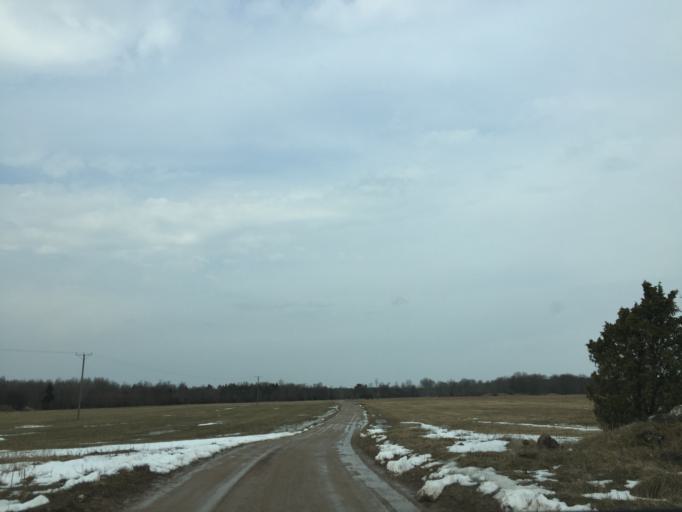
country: EE
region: Saare
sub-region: Kuressaare linn
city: Kuressaare
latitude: 58.4342
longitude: 22.1426
